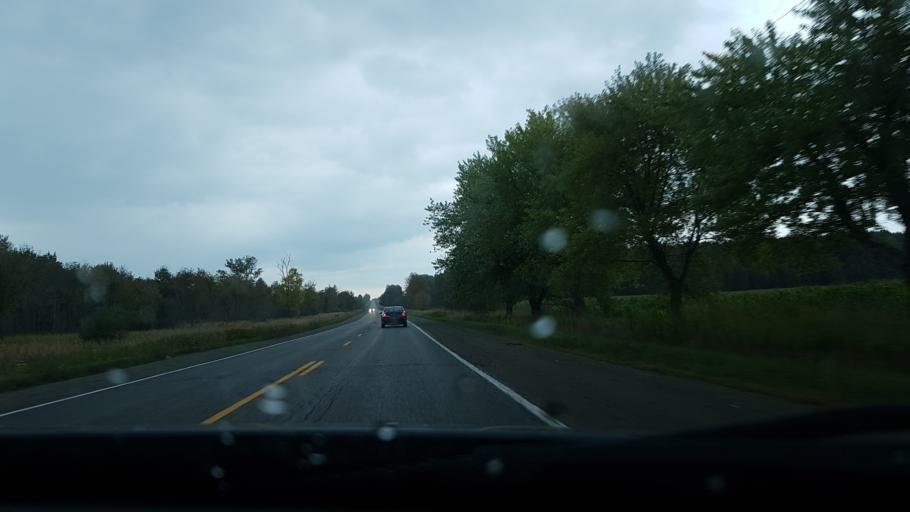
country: CA
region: Ontario
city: Omemee
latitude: 44.3762
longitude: -78.6332
